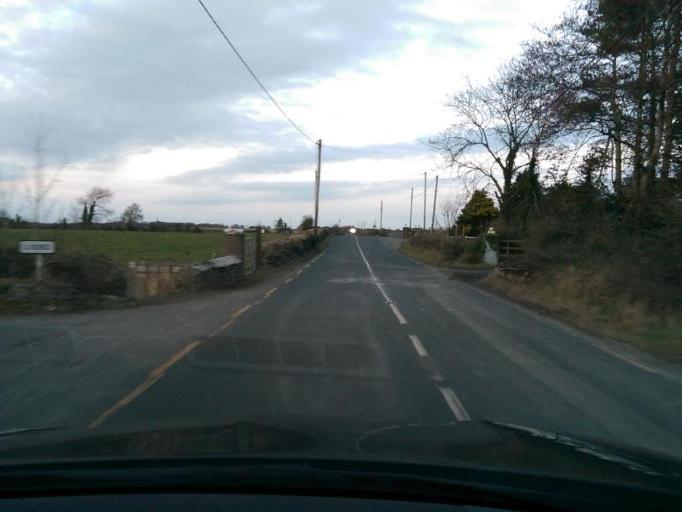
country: IE
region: Connaught
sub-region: County Galway
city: Portumna
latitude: 53.0503
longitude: -8.1048
